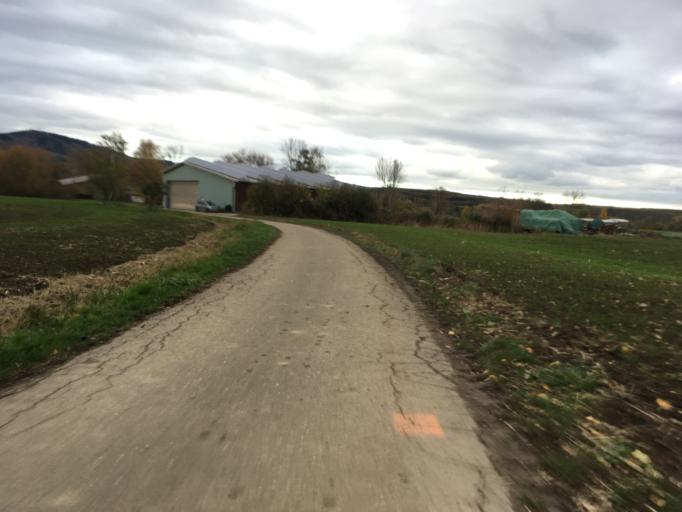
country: DE
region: Baden-Wuerttemberg
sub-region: Freiburg Region
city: Botzingen
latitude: 48.0700
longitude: 7.7334
